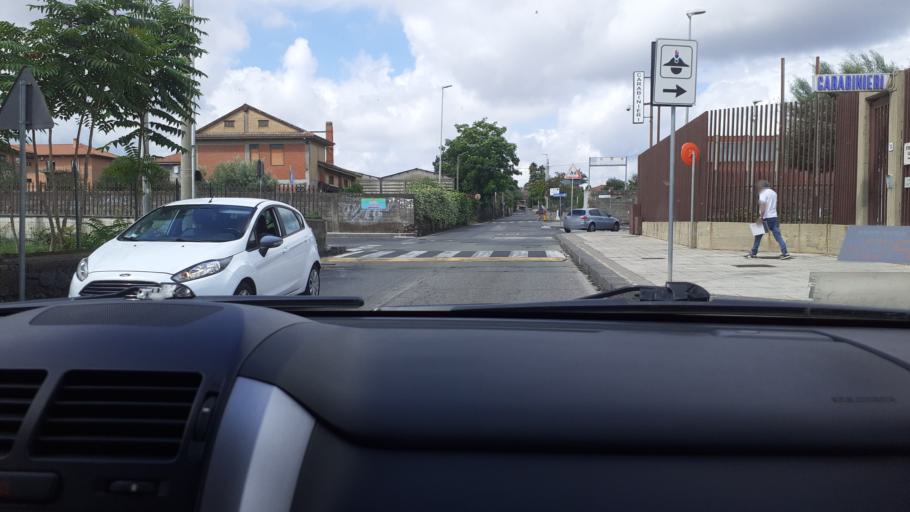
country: IT
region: Sicily
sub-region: Catania
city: San Giovanni la Punta
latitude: 37.5784
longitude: 15.1018
